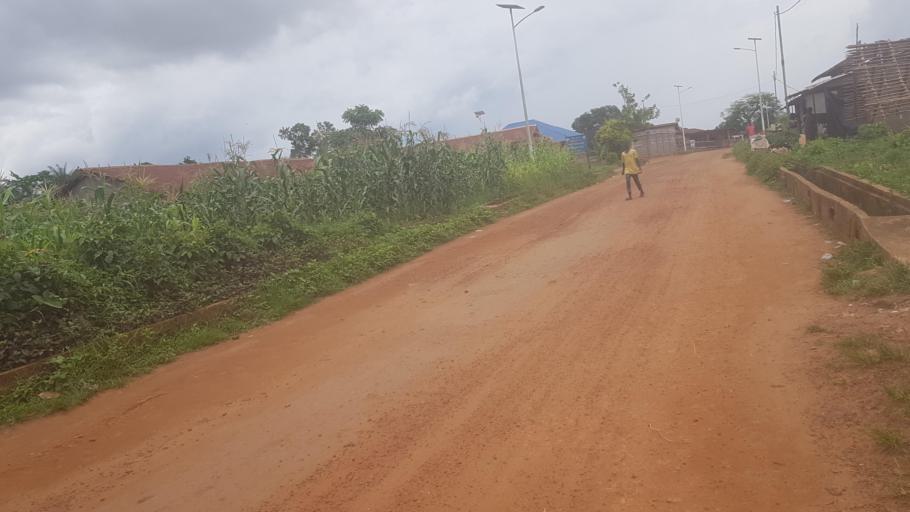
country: SL
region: Southern Province
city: Mogbwemo
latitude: 7.6113
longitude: -12.1805
